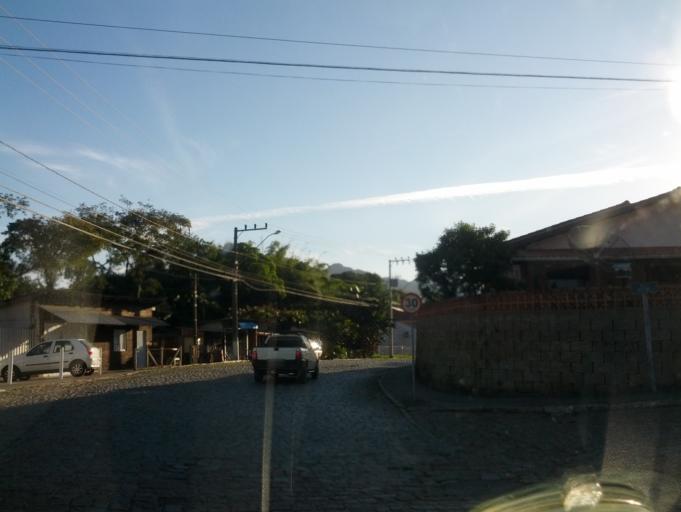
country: BR
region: Santa Catarina
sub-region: Indaial
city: Indaial
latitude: -26.8985
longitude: -49.2461
